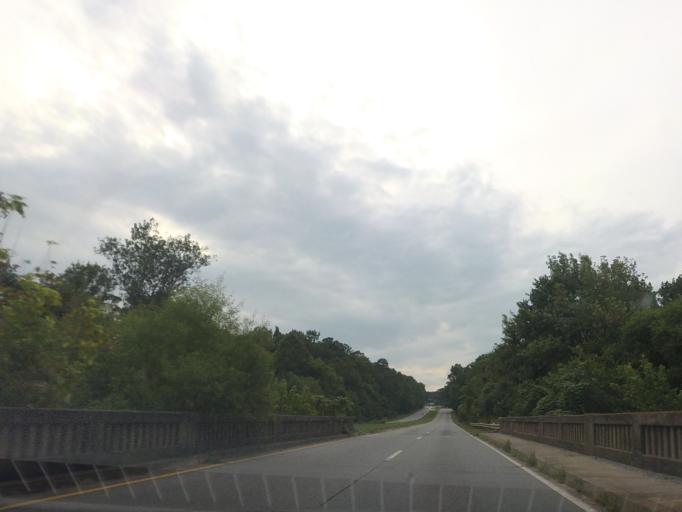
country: US
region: Georgia
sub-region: Bibb County
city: Macon
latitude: 32.8464
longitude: -83.5957
